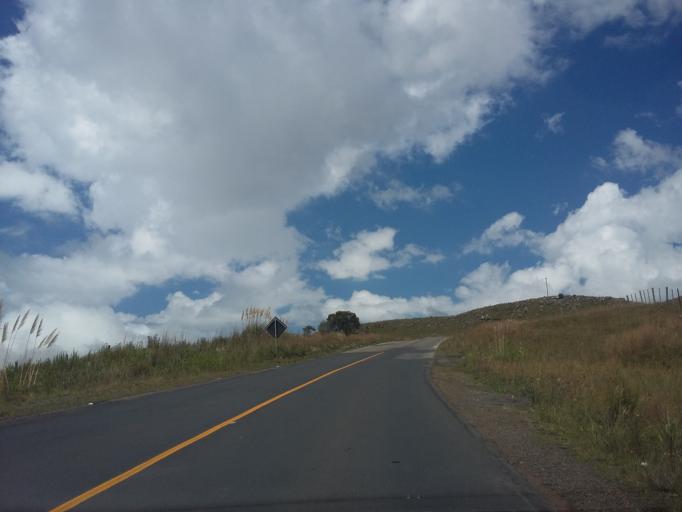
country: BR
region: Santa Catarina
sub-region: Lauro Muller
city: Lauro Muller
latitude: -28.3645
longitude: -49.5802
